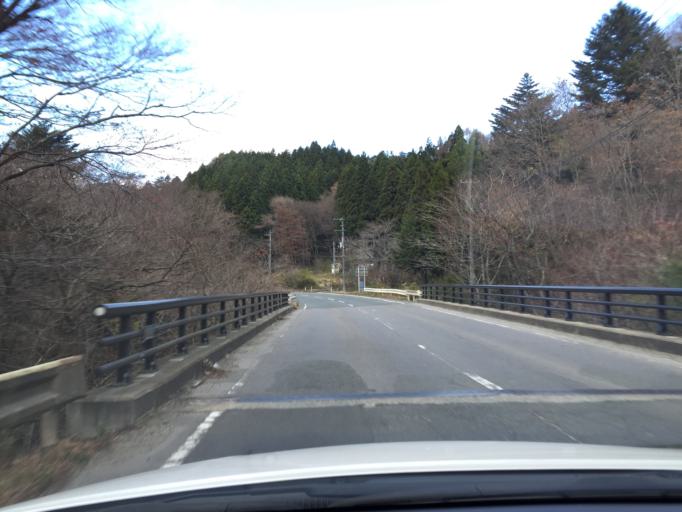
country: JP
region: Miyagi
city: Marumori
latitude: 37.6875
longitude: 140.8453
